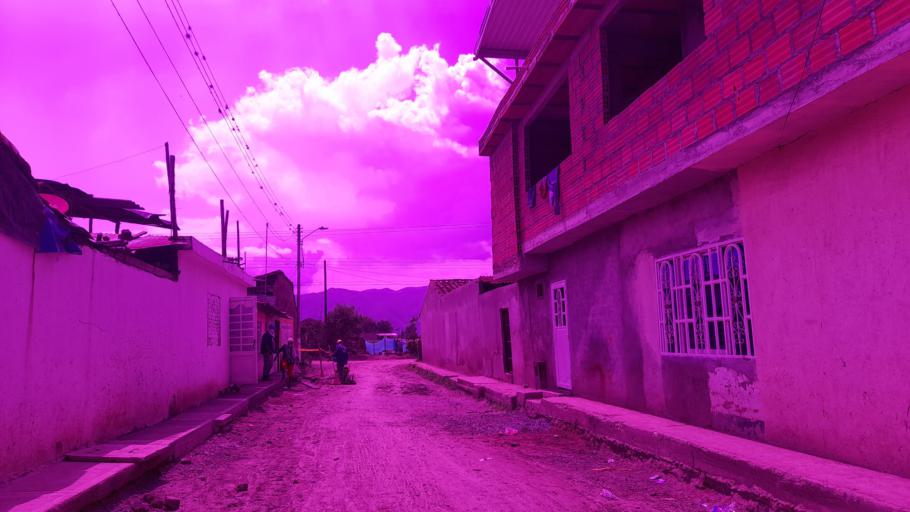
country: CO
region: Valle del Cauca
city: Guacari
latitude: 3.7612
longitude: -76.3680
